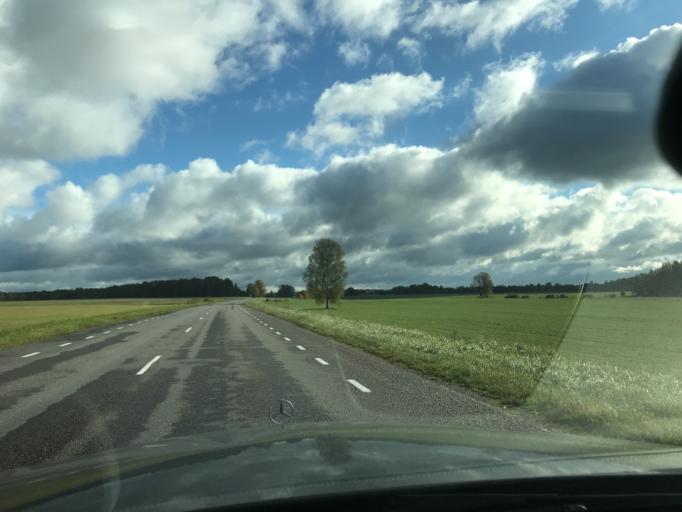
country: EE
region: Valgamaa
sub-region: Torva linn
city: Torva
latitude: 57.9790
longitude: 25.9634
